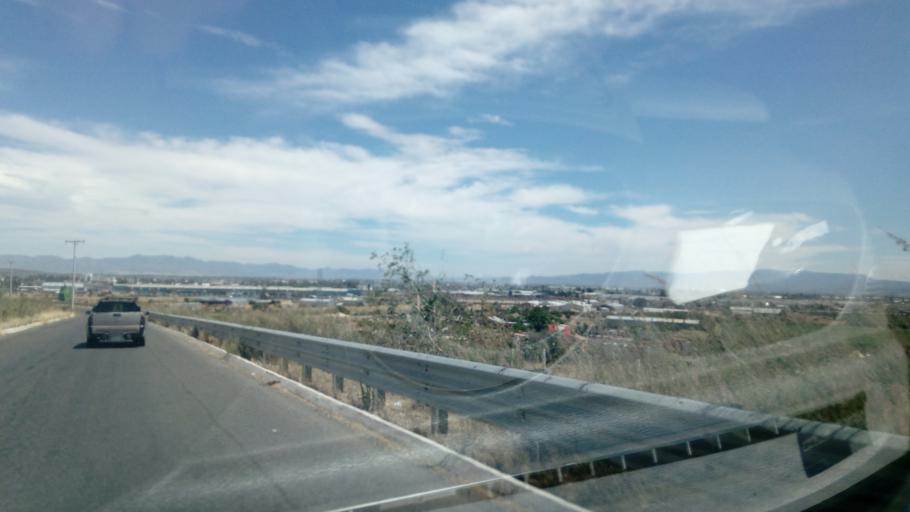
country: MX
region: Durango
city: Victoria de Durango
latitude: 24.0760
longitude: -104.6207
